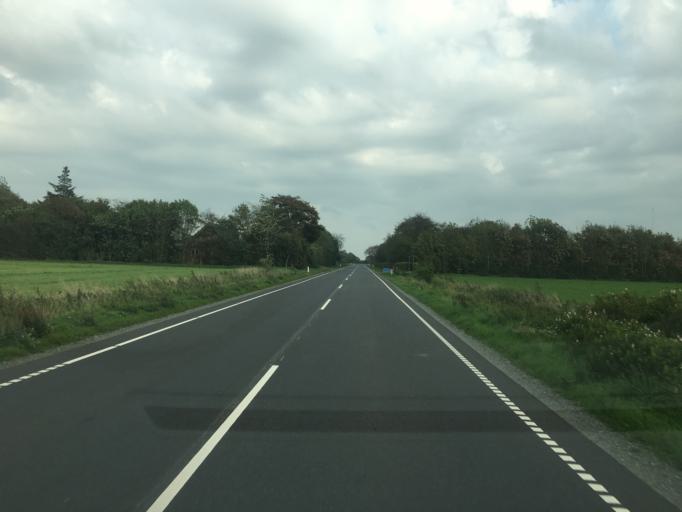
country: DK
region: South Denmark
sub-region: Tonder Kommune
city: Logumkloster
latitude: 54.9786
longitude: 9.0333
